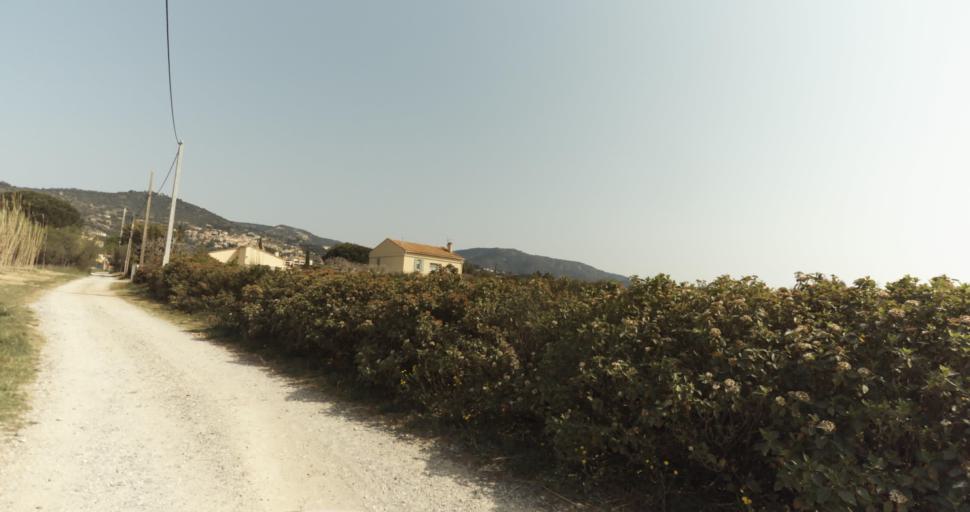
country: FR
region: Provence-Alpes-Cote d'Azur
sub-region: Departement du Var
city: Bormes-les-Mimosas
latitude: 43.1391
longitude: 6.3346
